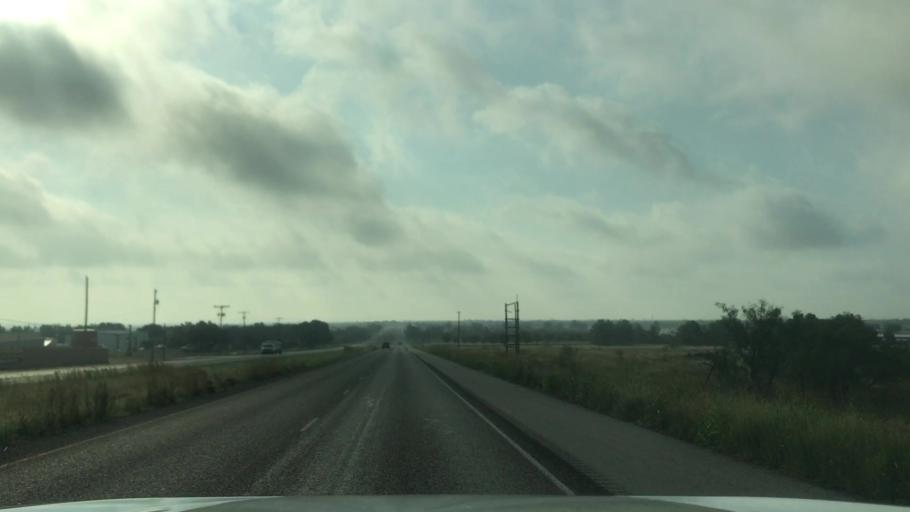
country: US
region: Texas
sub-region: Garza County
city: Post
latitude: 33.2081
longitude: -101.4032
